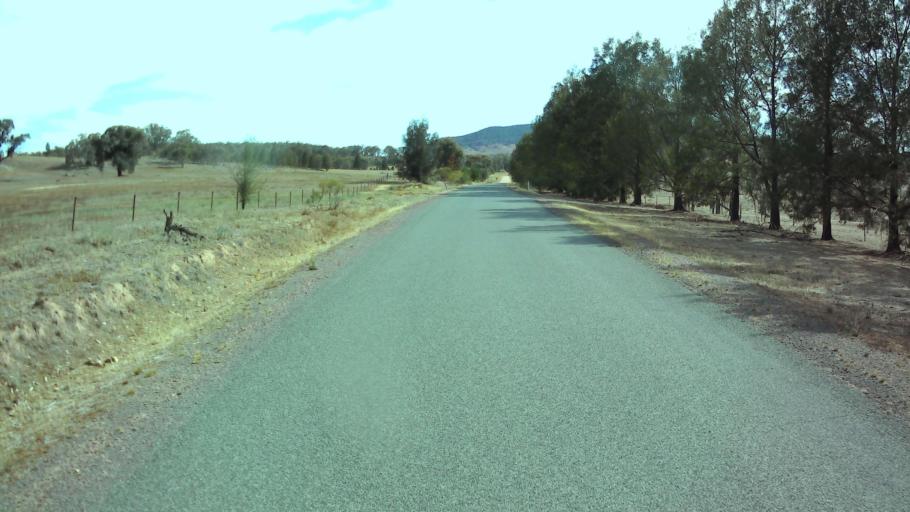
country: AU
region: New South Wales
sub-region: Weddin
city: Grenfell
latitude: -33.8105
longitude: 148.2929
